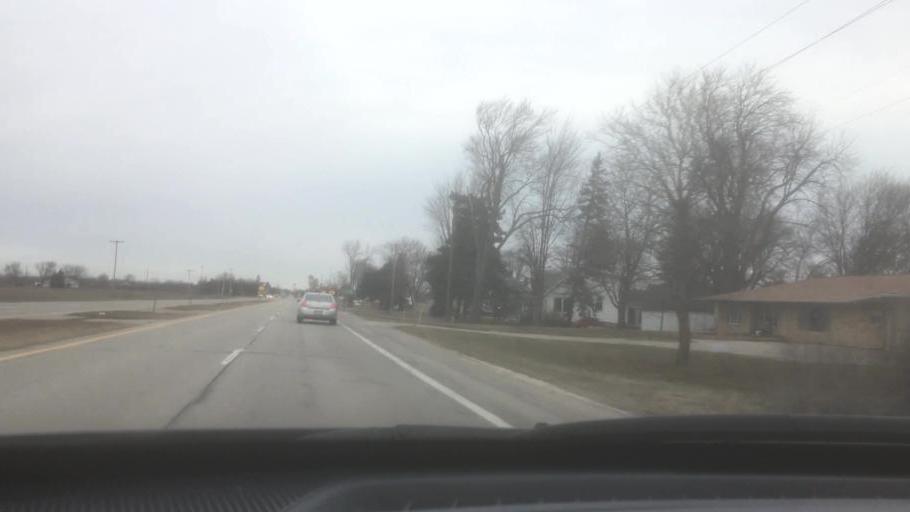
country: US
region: Michigan
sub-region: Bay County
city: Essexville
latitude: 43.5625
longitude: -83.8416
